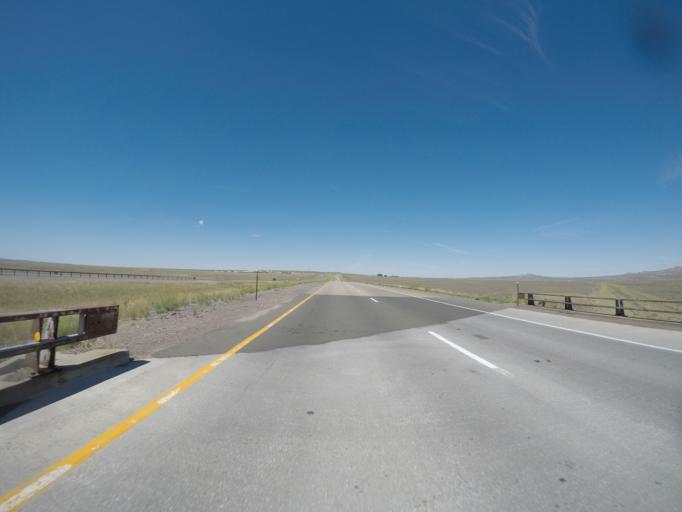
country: US
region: Wyoming
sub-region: Carbon County
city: Saratoga
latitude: 41.7420
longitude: -106.8069
